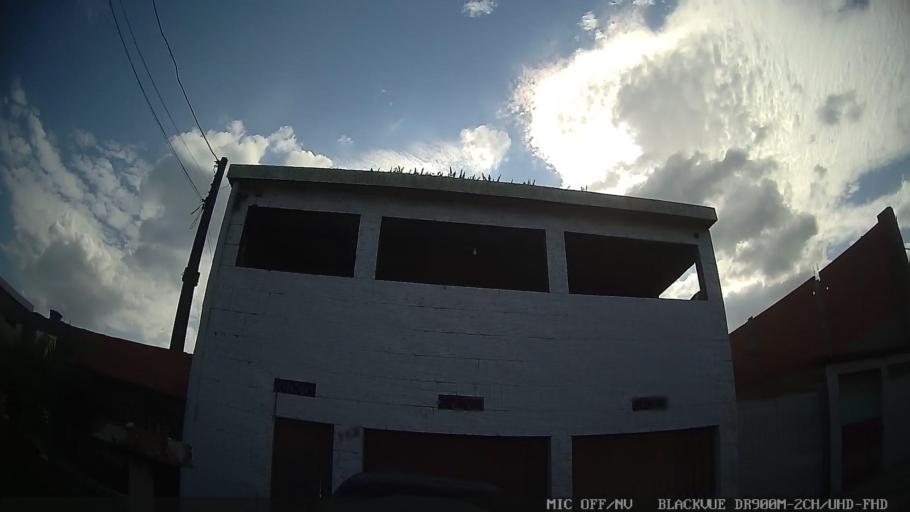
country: BR
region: Sao Paulo
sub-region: Guaruja
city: Guaruja
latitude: -23.9745
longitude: -46.2147
